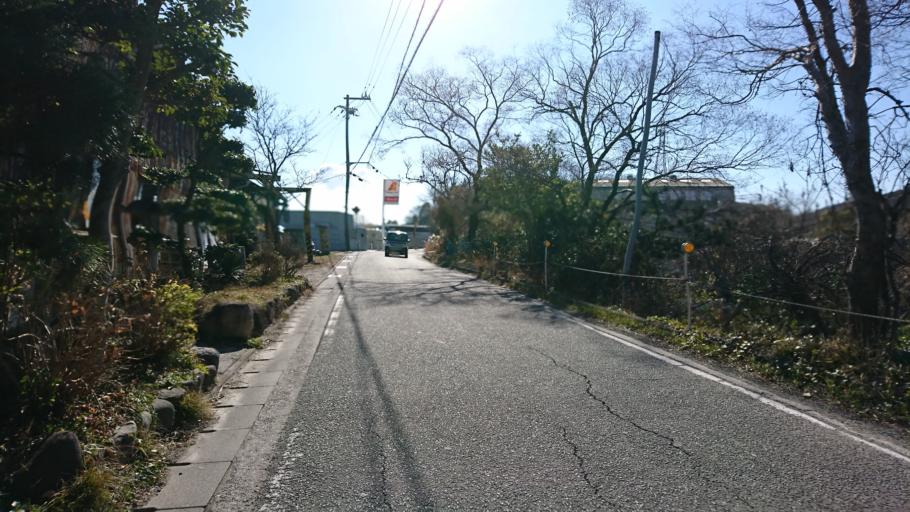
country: JP
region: Hyogo
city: Kakogawacho-honmachi
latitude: 34.7895
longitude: 134.7965
